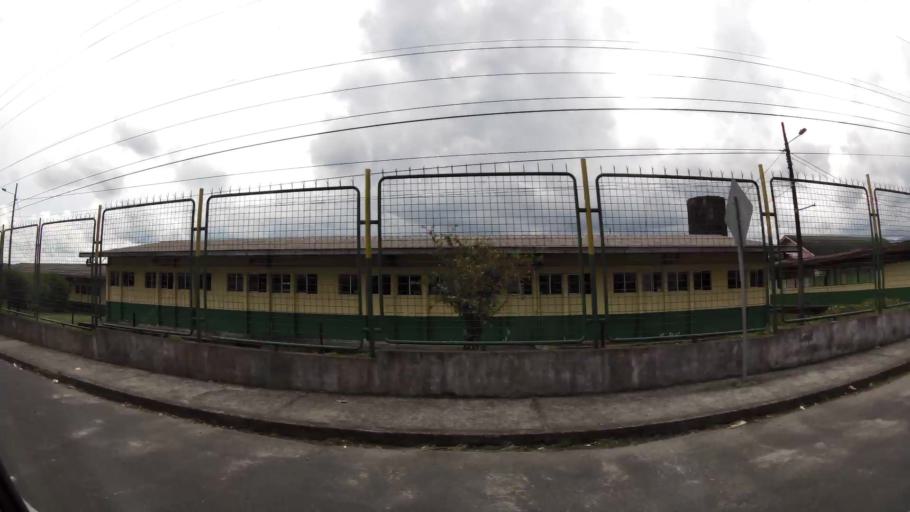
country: EC
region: Pastaza
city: Puyo
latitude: -1.5049
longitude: -78.0608
